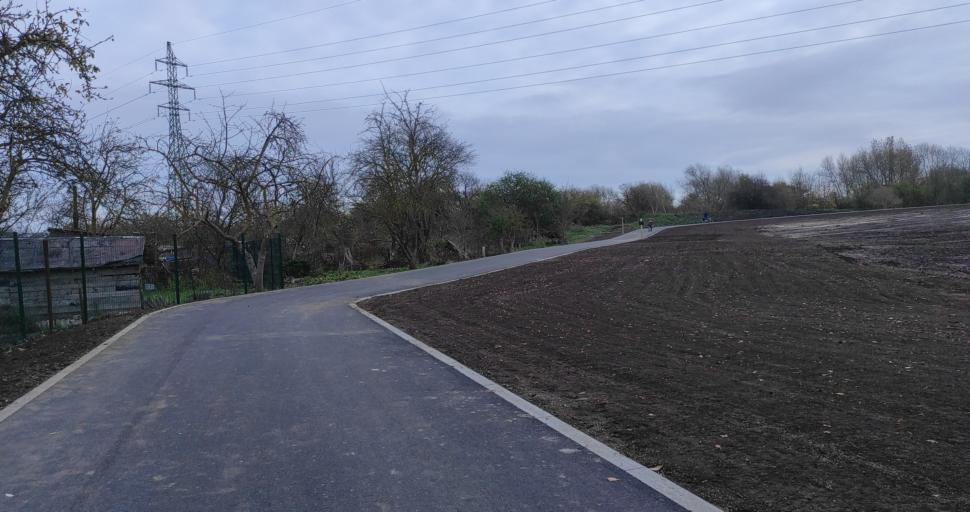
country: LV
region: Liepaja
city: Liepaja
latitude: 56.5174
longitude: 21.0367
